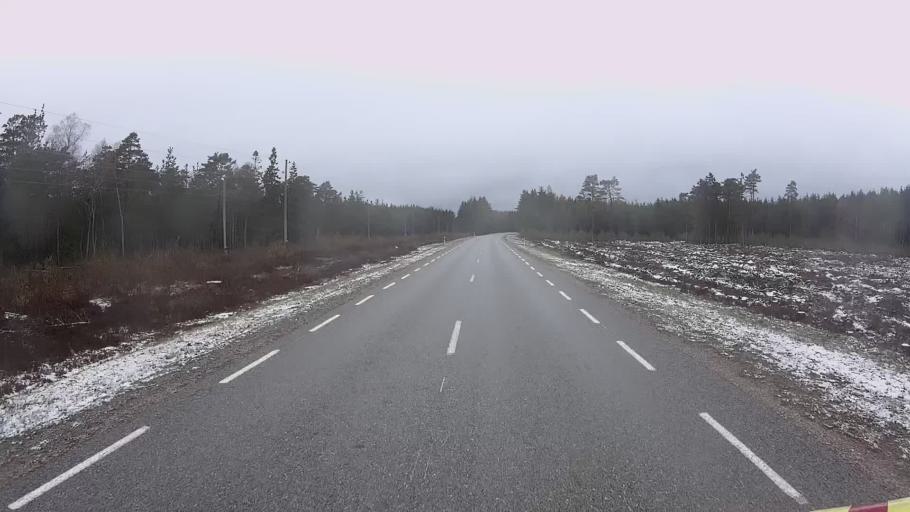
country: EE
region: Hiiumaa
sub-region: Kaerdla linn
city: Kardla
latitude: 59.0249
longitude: 22.6721
